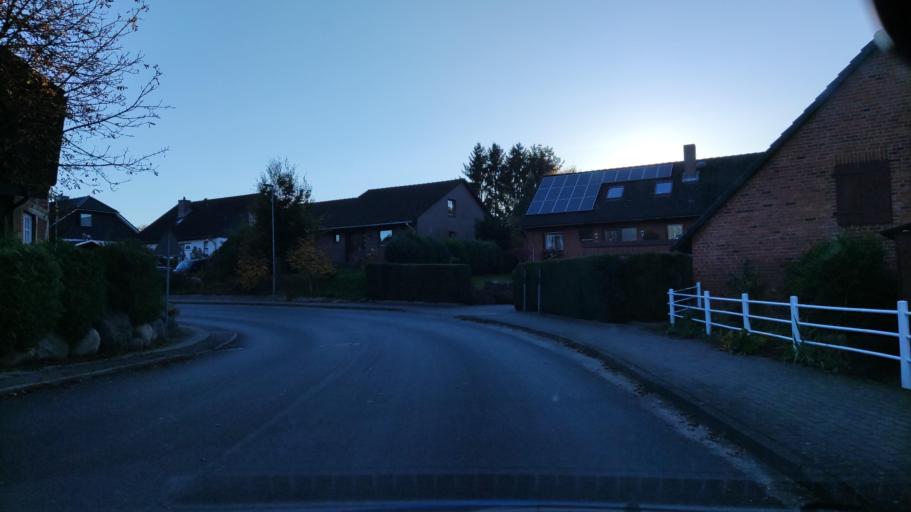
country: DE
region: Schleswig-Holstein
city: Dahmker
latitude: 53.5972
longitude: 10.4479
